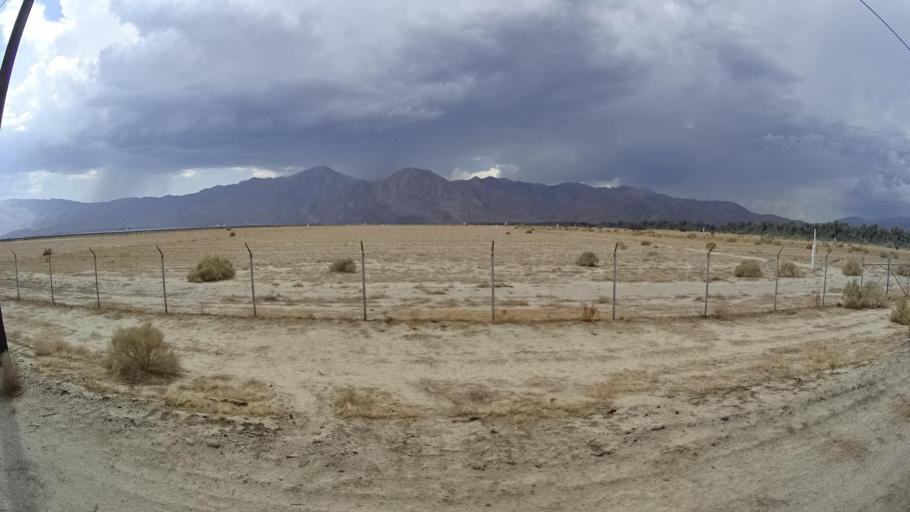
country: US
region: California
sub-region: San Diego County
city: Borrego Springs
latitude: 33.2971
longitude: -116.3490
